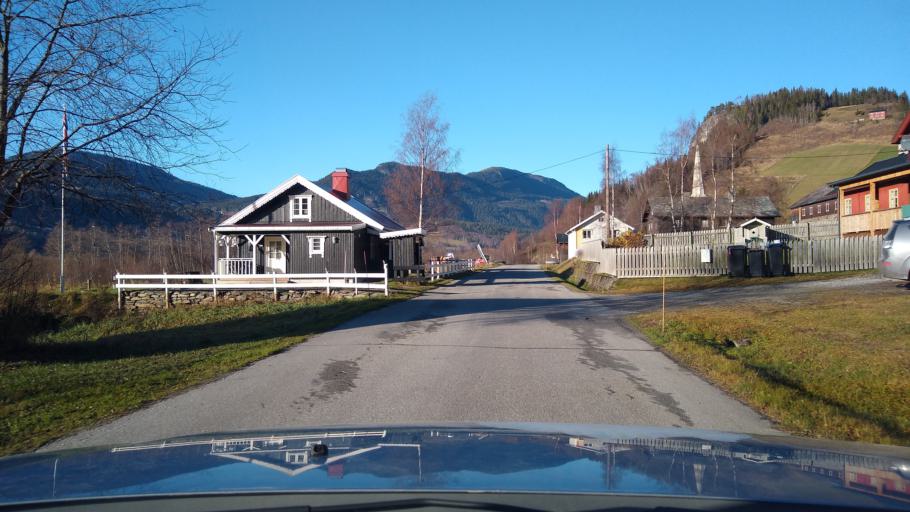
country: NO
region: Oppland
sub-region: Ringebu
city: Ringebu
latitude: 61.4259
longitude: 10.2223
